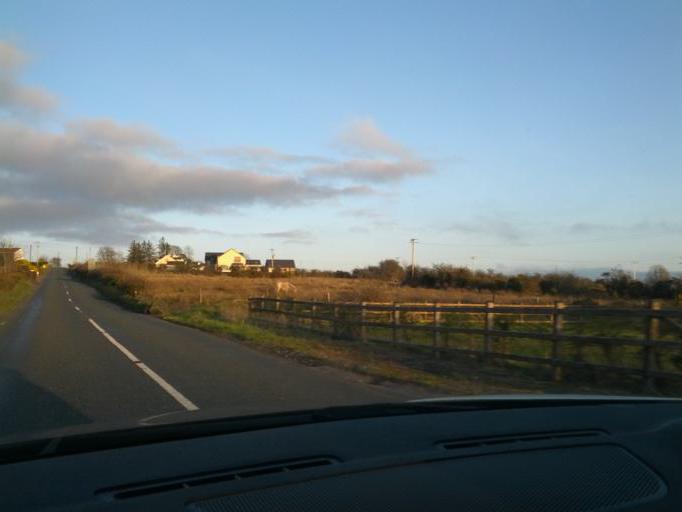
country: IE
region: Connaught
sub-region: Sligo
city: Tobercurry
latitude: 54.0473
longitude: -8.6874
